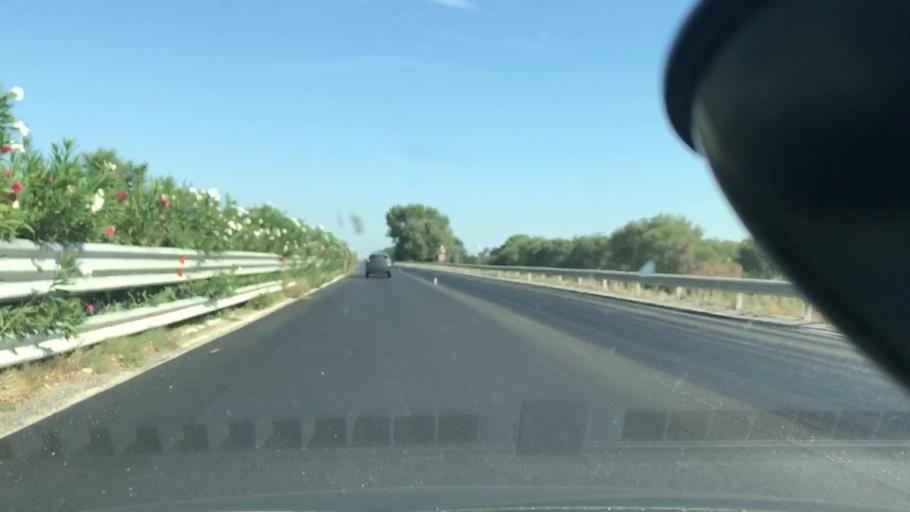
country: IT
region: Apulia
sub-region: Provincia di Foggia
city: Ascoli Satriano
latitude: 41.2723
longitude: 15.5528
